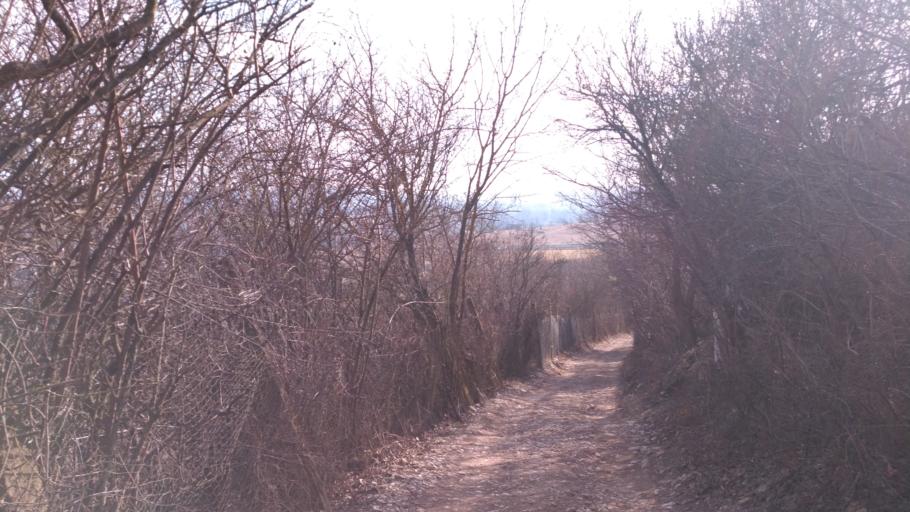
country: SK
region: Kosicky
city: Medzev
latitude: 48.6075
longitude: 20.8758
